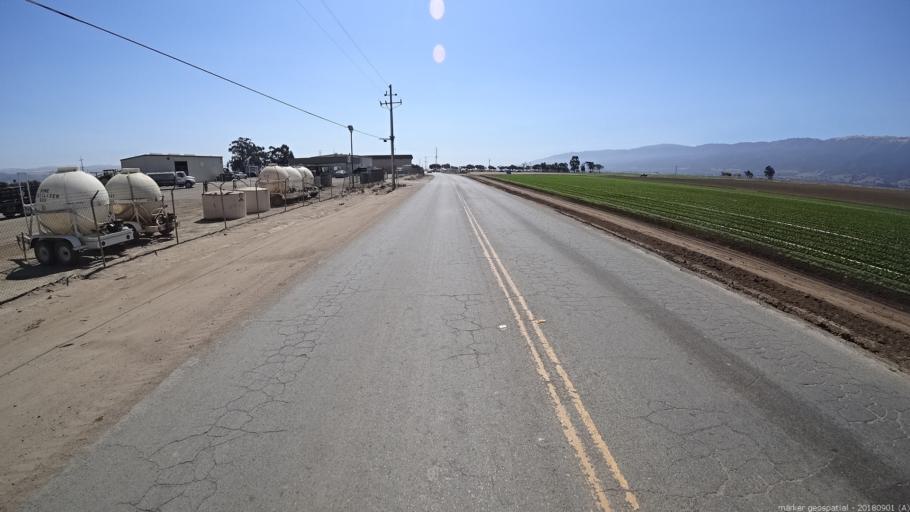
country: US
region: California
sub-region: Monterey County
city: Chualar
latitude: 36.5675
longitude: -121.5182
